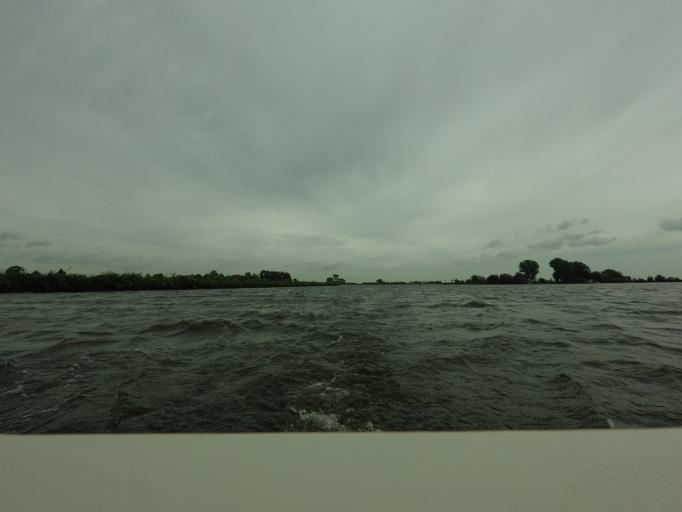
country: NL
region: Friesland
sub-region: Gemeente Boarnsterhim
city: Grou
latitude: 53.1051
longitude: 5.8547
